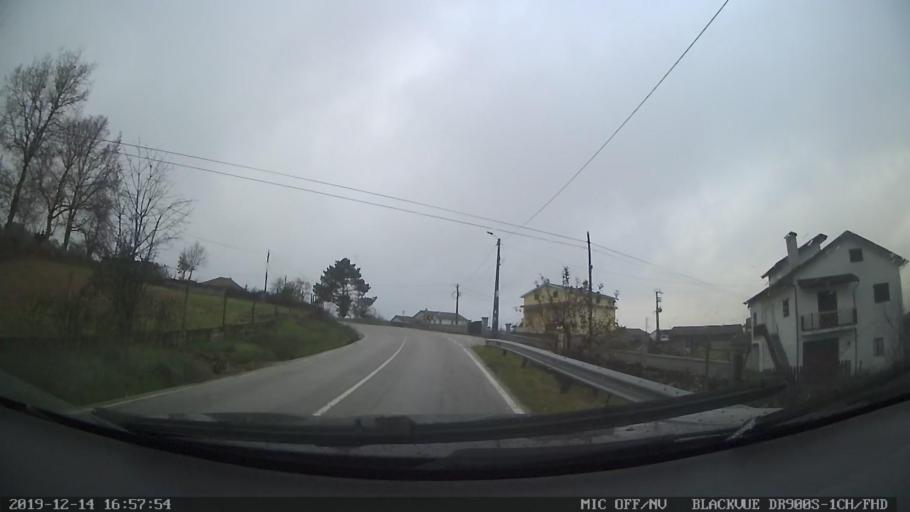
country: PT
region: Vila Real
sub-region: Murca
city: Murca
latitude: 41.4391
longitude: -7.5499
